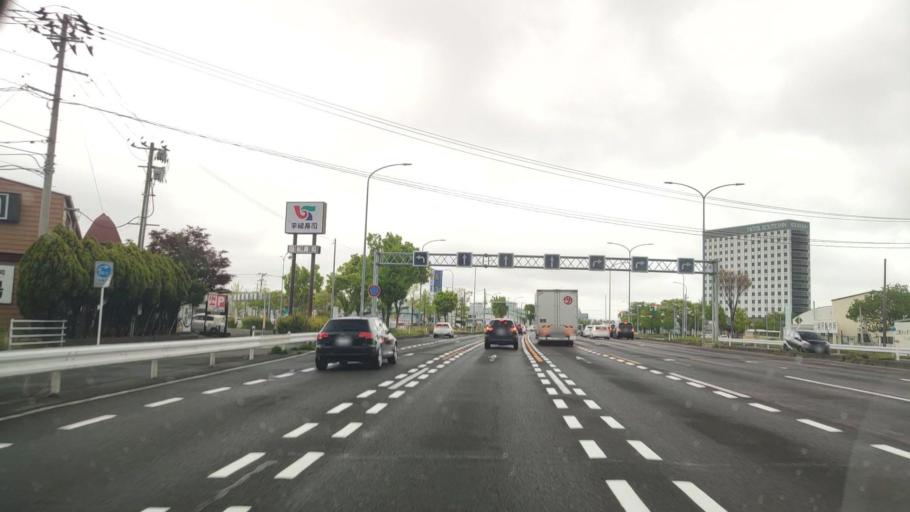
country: JP
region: Miyagi
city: Sendai-shi
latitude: 38.2500
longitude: 140.9270
